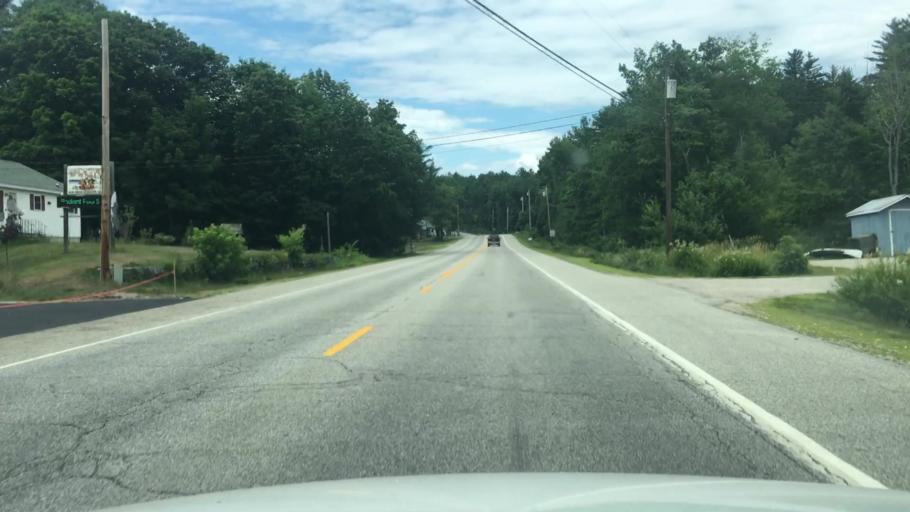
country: US
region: Maine
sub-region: Oxford County
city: West Paris
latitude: 44.3348
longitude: -70.5562
